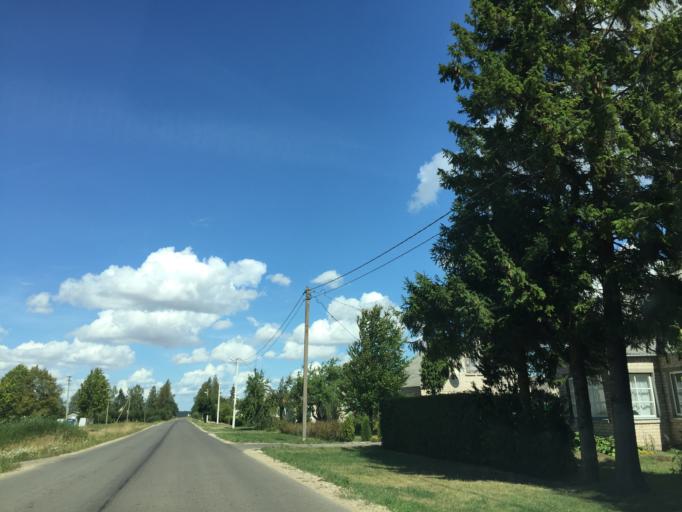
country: LV
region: Rundales
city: Pilsrundale
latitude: 56.3173
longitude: 23.9119
